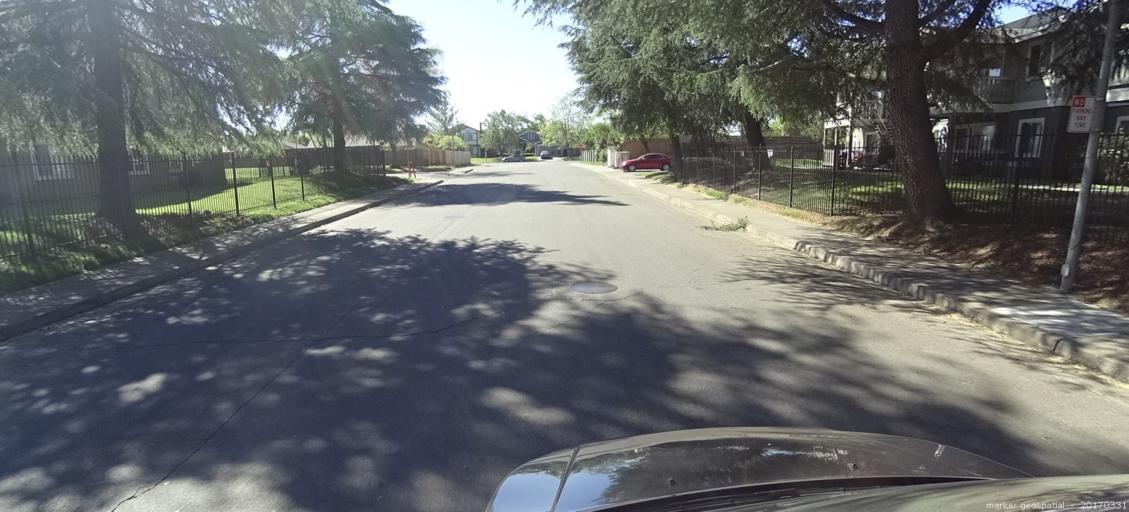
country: US
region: California
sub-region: Sacramento County
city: Parkway
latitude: 38.4736
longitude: -121.4418
